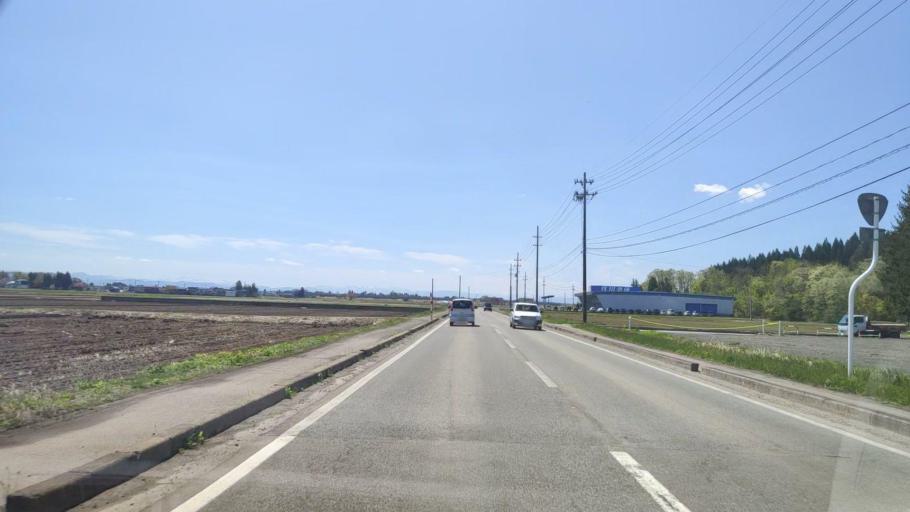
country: JP
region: Akita
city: Omagari
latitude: 39.4431
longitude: 140.4483
